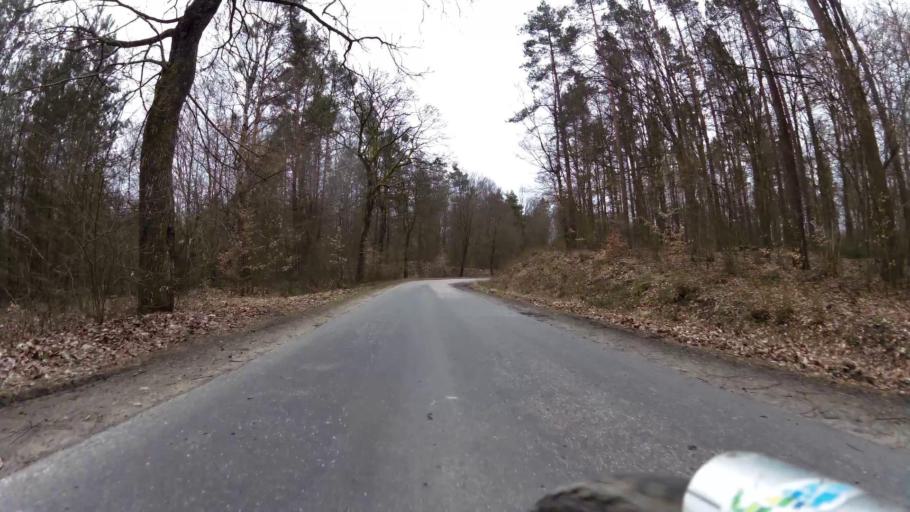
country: PL
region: Pomeranian Voivodeship
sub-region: Powiat bytowski
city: Trzebielino
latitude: 54.0978
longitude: 17.1336
